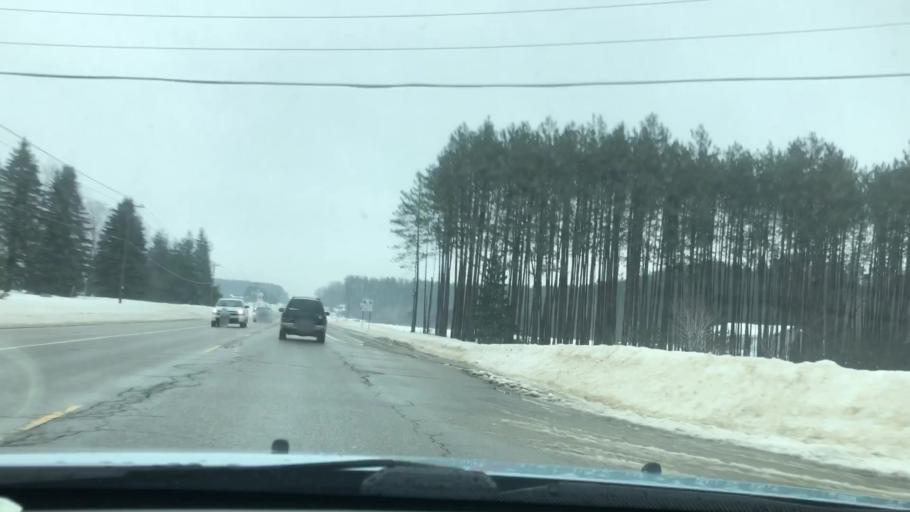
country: US
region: Michigan
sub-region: Otsego County
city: Gaylord
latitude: 45.0276
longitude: -84.7460
